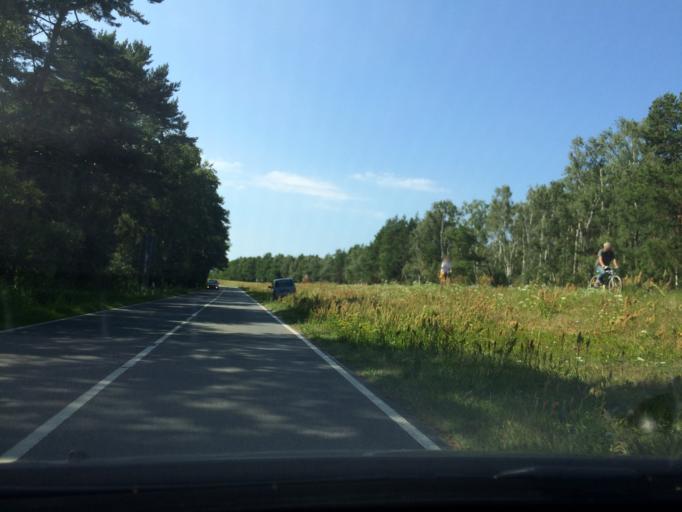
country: DE
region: Mecklenburg-Vorpommern
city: Ostseebad Prerow
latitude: 54.4485
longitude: 12.6047
